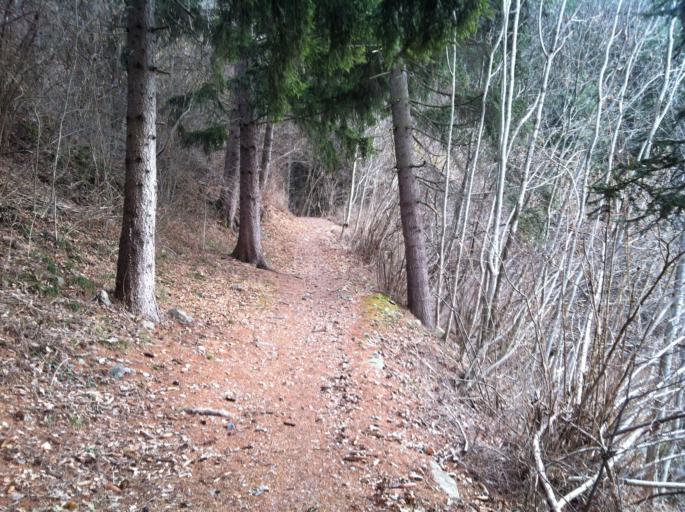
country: IT
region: Trentino-Alto Adige
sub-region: Bolzano
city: Bressanone
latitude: 46.6941
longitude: 11.6632
